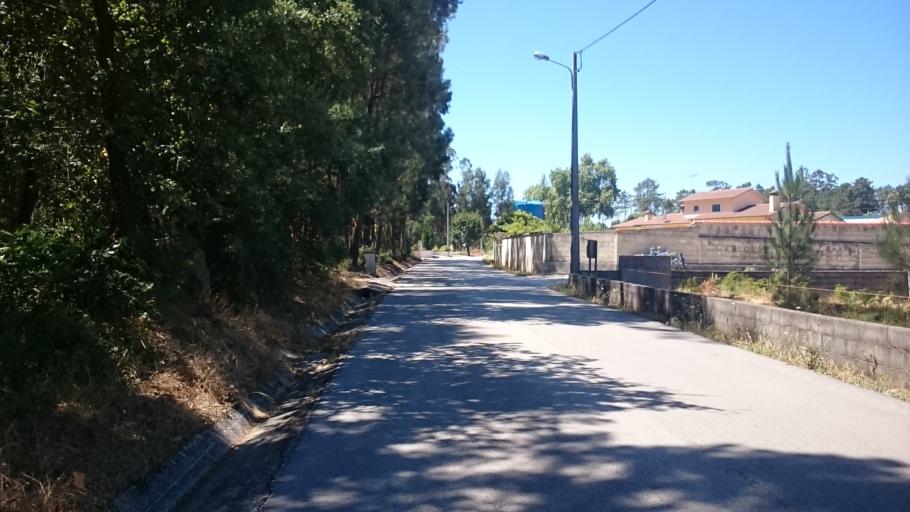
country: PT
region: Leiria
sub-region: Leiria
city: Souto da Carpalhosa
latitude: 39.8239
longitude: -8.8377
